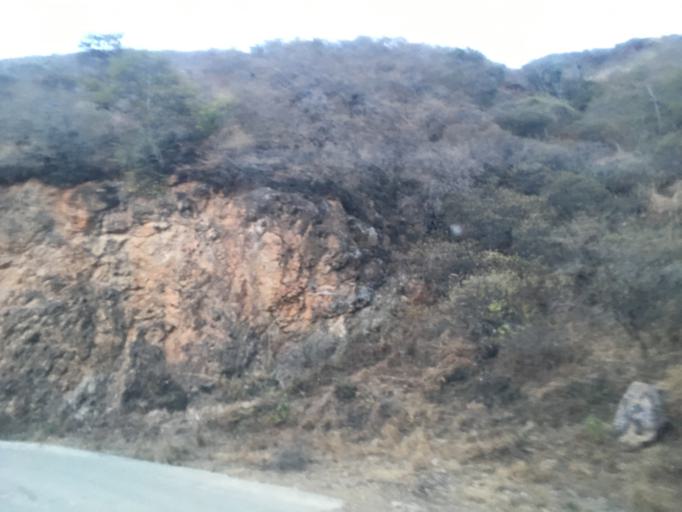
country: CO
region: Santander
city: Aratoca
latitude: 6.7932
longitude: -72.9976
